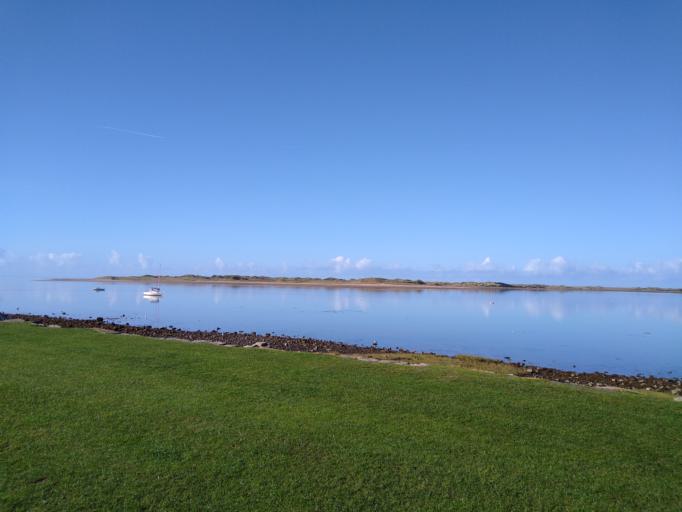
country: GB
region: England
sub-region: Cumbria
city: Seascale
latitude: 54.3555
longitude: -3.4108
